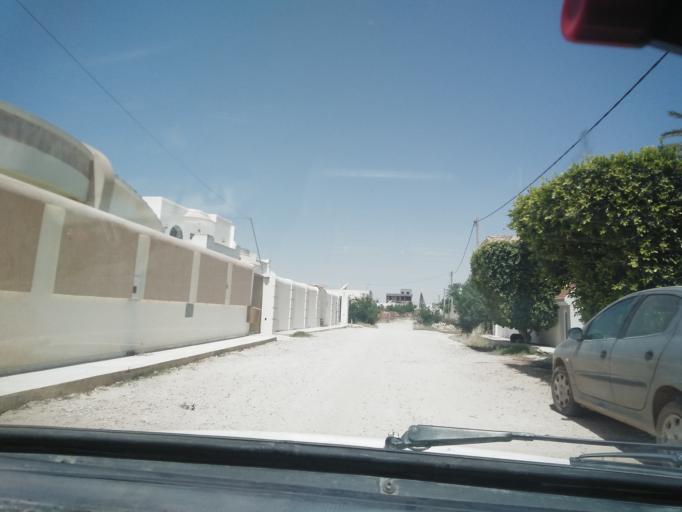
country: TN
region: Safaqis
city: Al Qarmadah
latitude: 34.8052
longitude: 10.7740
